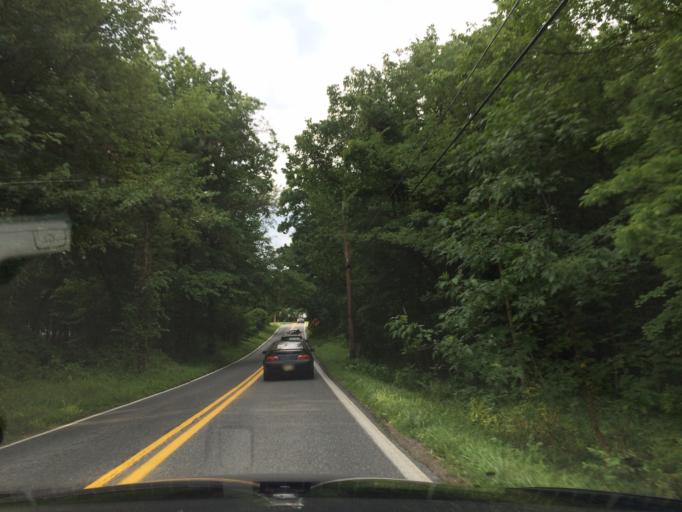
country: US
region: Maryland
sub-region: Montgomery County
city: Clarksburg
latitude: 39.2568
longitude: -77.2758
